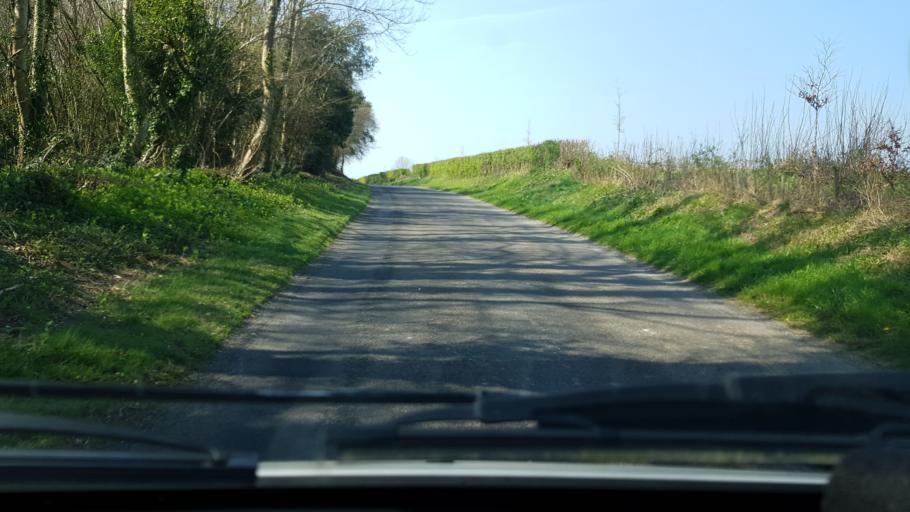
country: GB
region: England
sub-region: West Sussex
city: Boxgrove
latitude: 50.8764
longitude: -0.7507
